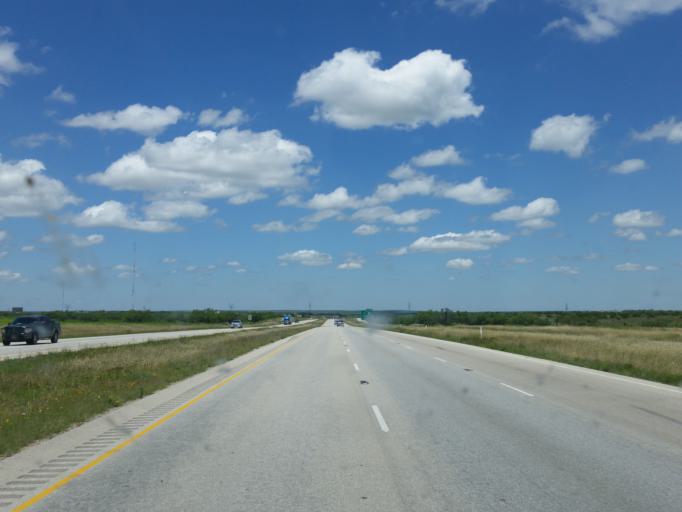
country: US
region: Texas
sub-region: Nolan County
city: Sweetwater
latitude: 32.4690
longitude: -100.3784
